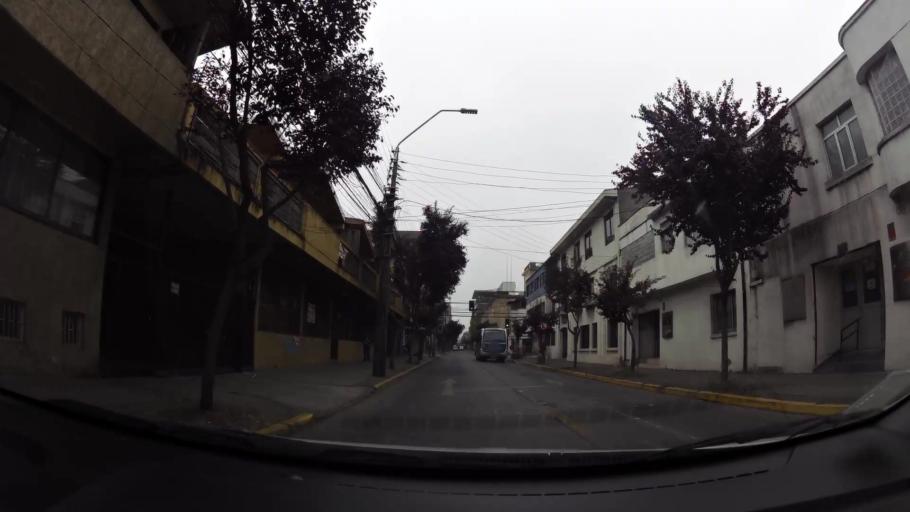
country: CL
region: Biobio
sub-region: Provincia de Concepcion
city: Concepcion
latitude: -36.8306
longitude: -73.0542
